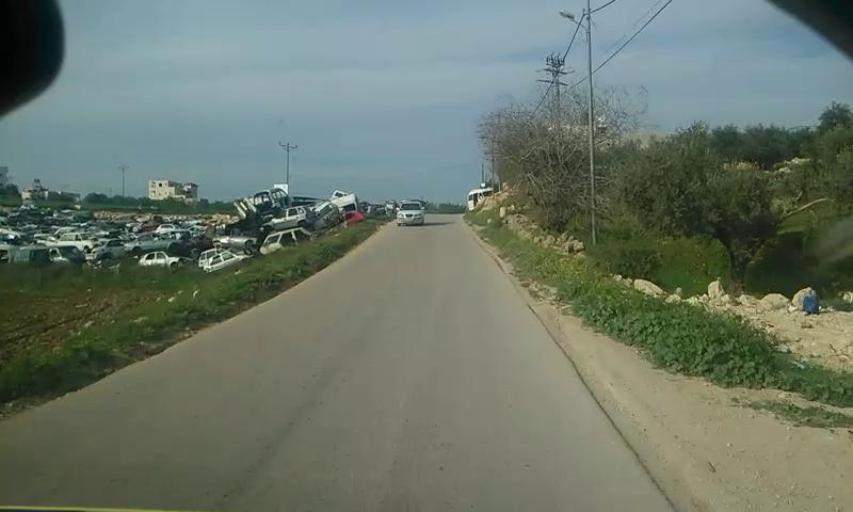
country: PS
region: West Bank
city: Bayt Ula
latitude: 31.6063
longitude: 35.0153
